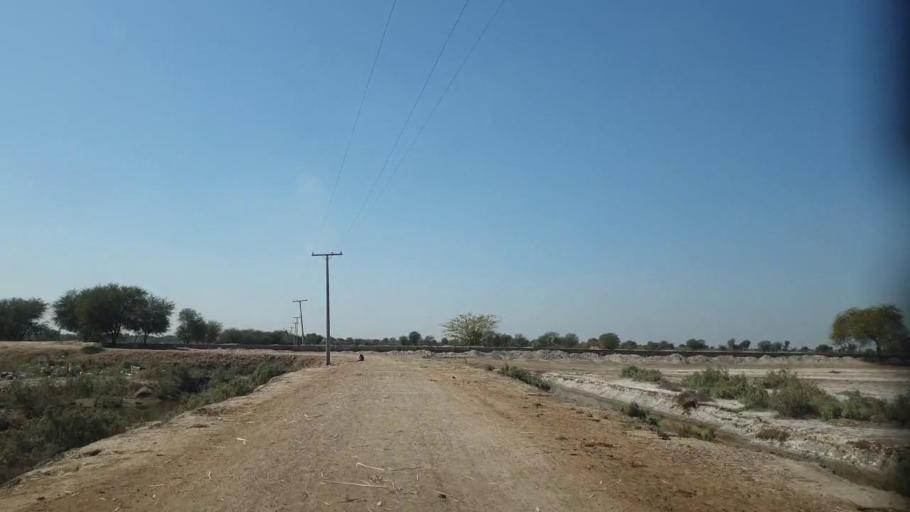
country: PK
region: Sindh
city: Mirpur Khas
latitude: 25.5809
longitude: 69.1108
